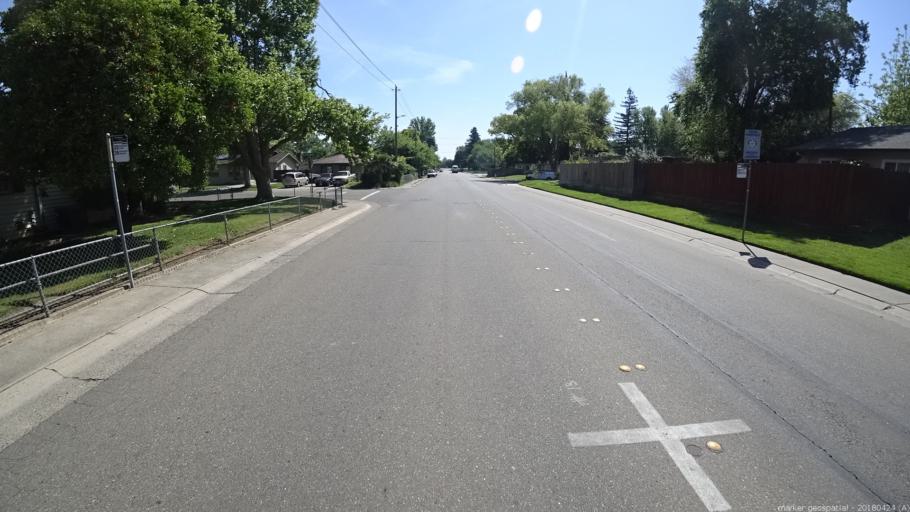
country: US
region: California
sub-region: Yolo County
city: West Sacramento
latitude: 38.5631
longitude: -121.5324
